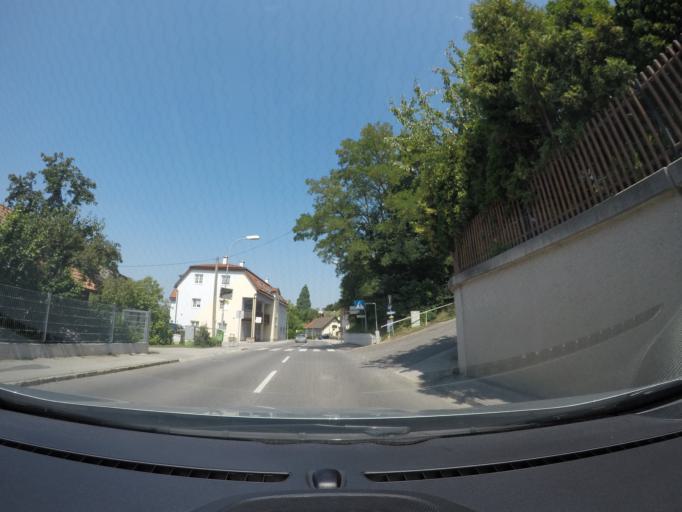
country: AT
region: Lower Austria
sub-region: Politischer Bezirk Sankt Polten
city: Eichgraben
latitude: 48.1795
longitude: 15.9852
